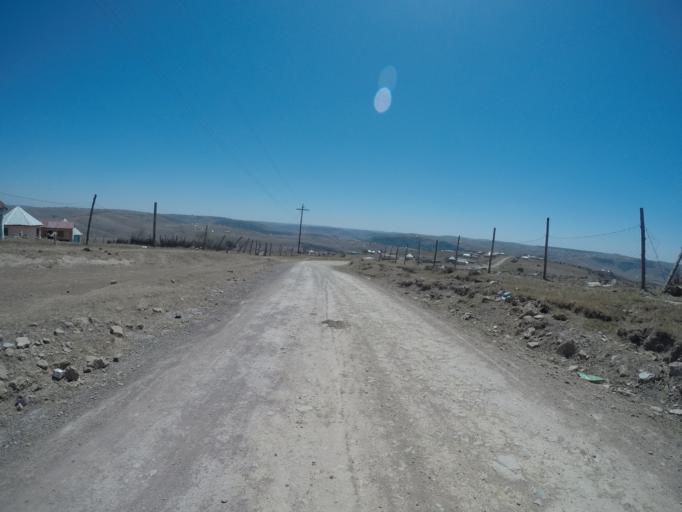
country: ZA
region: Eastern Cape
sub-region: OR Tambo District Municipality
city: Mthatha
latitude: -31.8870
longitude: 28.8757
